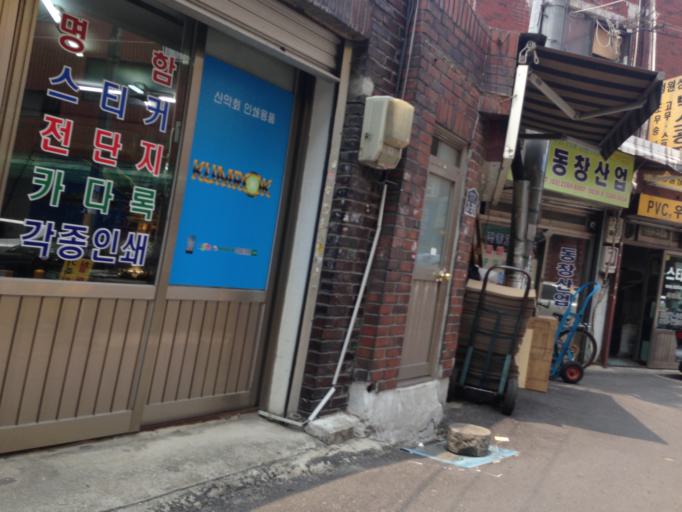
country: KR
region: Seoul
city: Seoul
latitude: 37.5677
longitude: 127.0003
